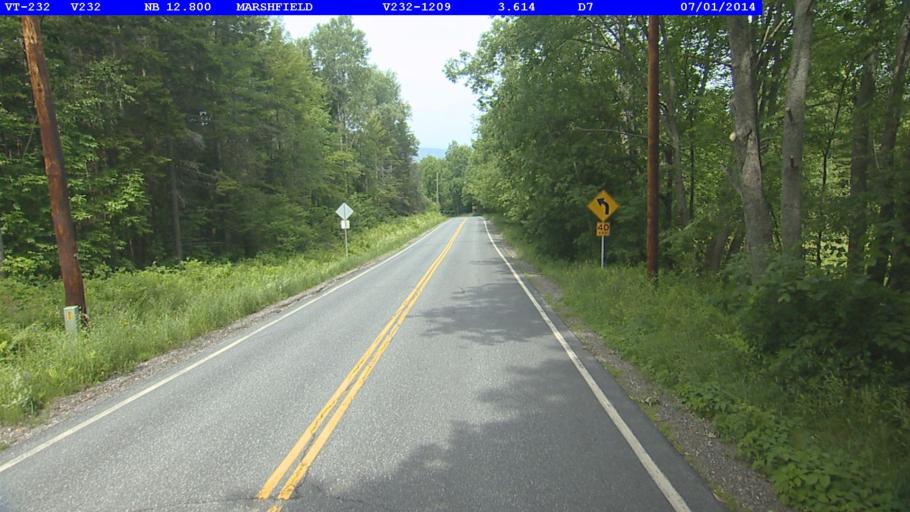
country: US
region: Vermont
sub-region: Caledonia County
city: Hardwick
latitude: 44.3579
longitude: -72.3148
